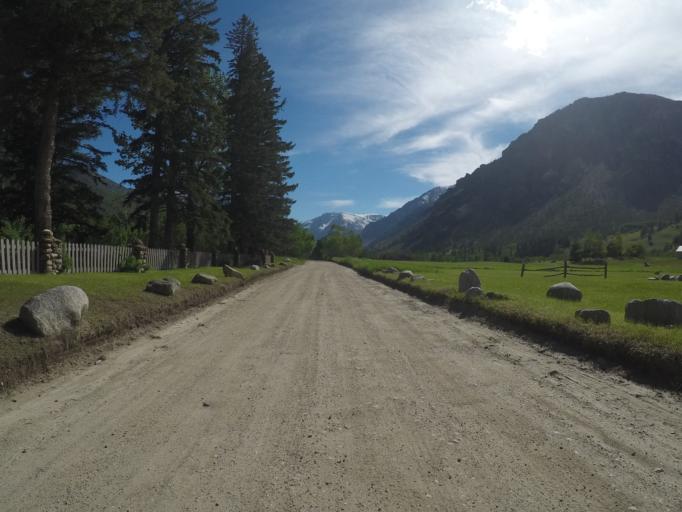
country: US
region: Montana
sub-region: Stillwater County
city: Absarokee
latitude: 45.2670
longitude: -109.5602
